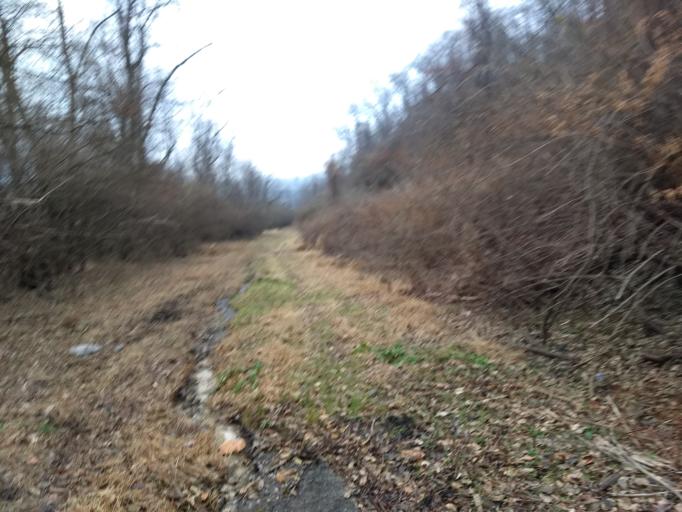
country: US
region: Pennsylvania
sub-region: Allegheny County
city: East Pittsburgh
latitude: 40.3881
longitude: -79.8472
